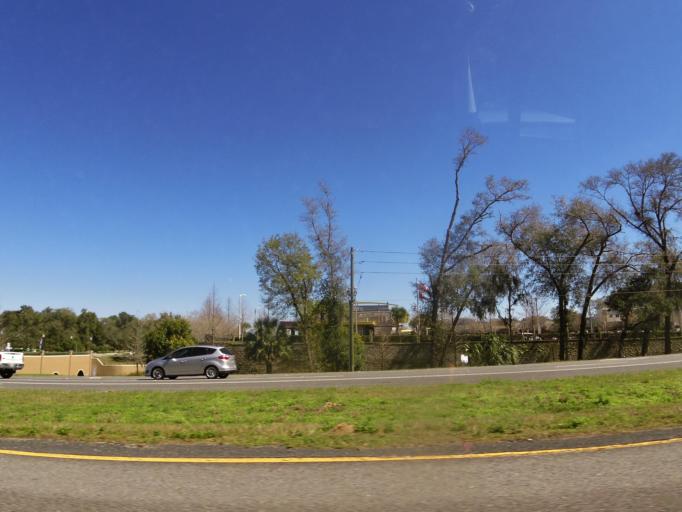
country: US
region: Florida
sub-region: Orange County
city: Tangerine
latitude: 28.7808
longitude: -81.6246
